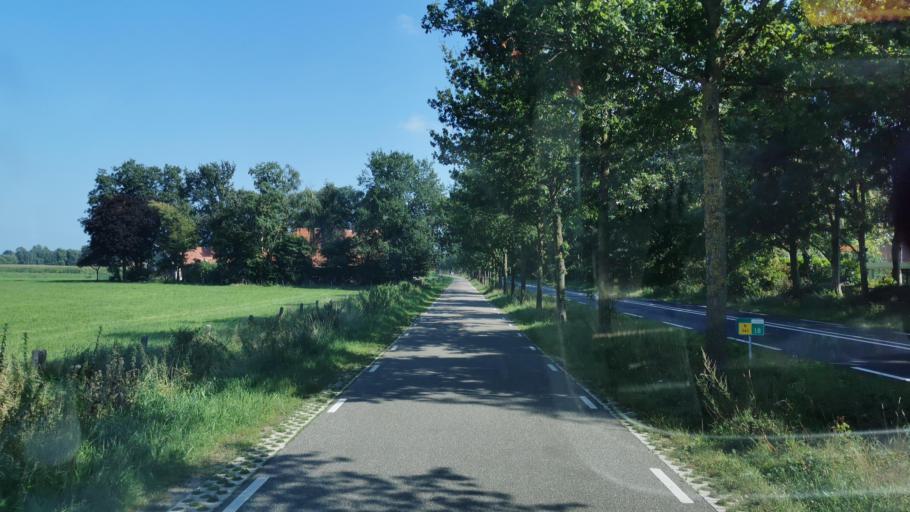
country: NL
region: Overijssel
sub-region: Gemeente Oldenzaal
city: Oldenzaal
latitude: 52.3304
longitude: 6.9215
